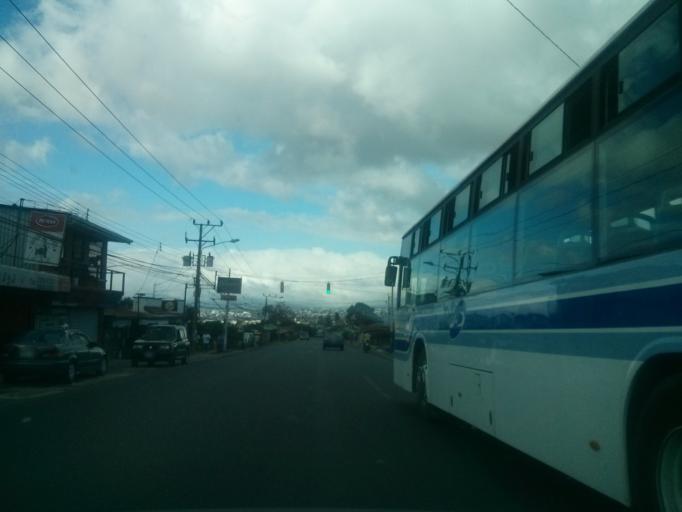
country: CR
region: San Jose
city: San Rafael Arriba
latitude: 9.8774
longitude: -84.0752
